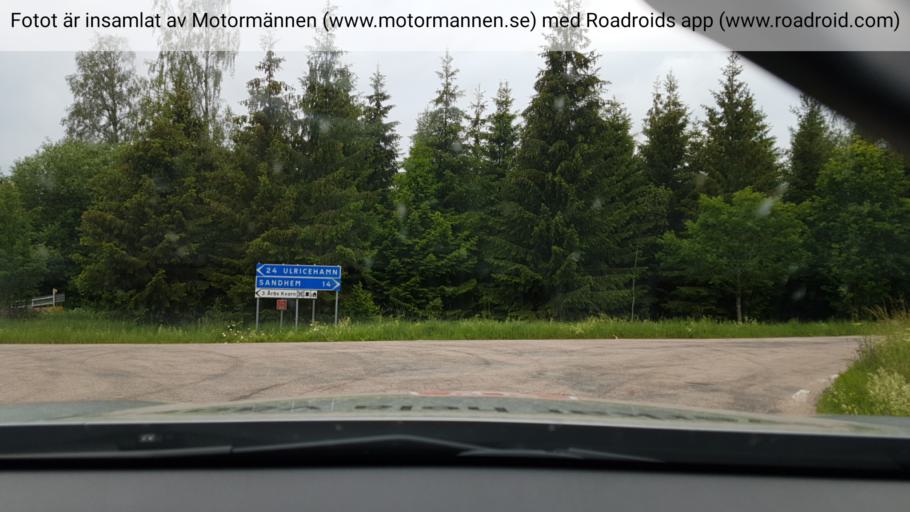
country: SE
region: Joenkoeping
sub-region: Mullsjo Kommun
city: Mullsjoe
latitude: 57.9106
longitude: 13.6618
